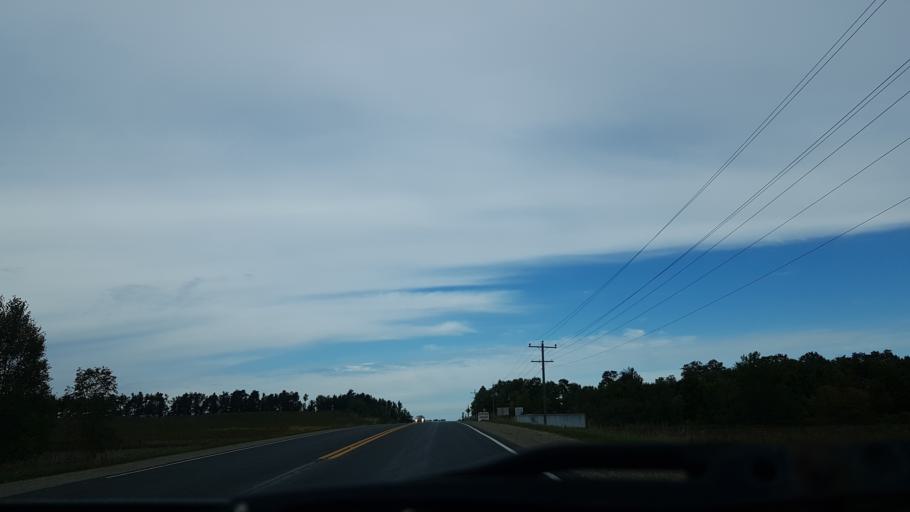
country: CA
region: Ontario
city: Angus
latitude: 44.3299
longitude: -80.0768
